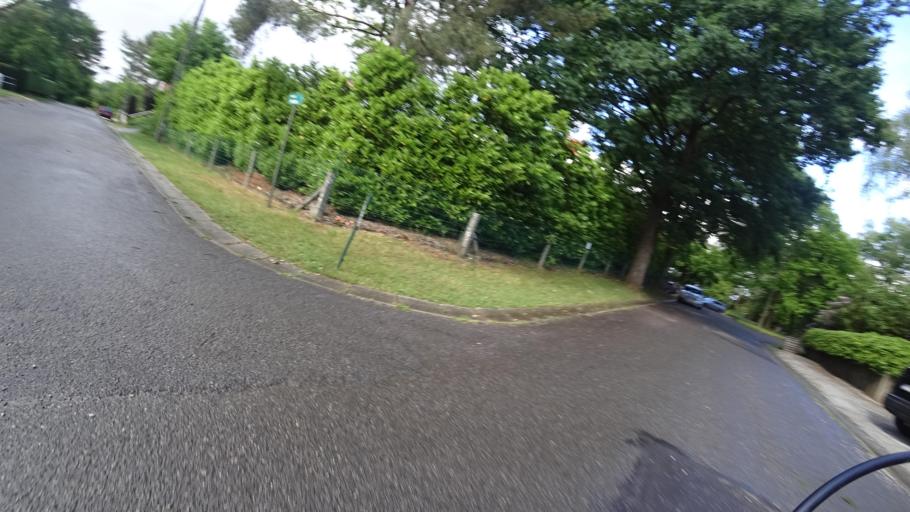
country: BE
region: Wallonia
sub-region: Province du Brabant Wallon
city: Wavre
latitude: 50.7005
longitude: 4.6127
